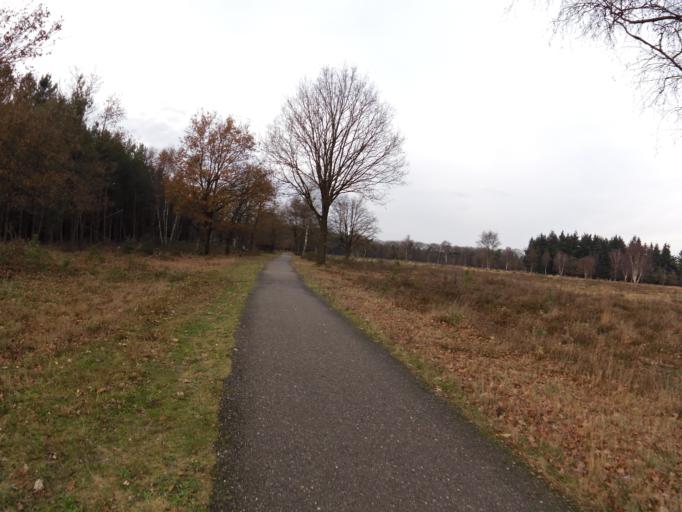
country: NL
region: North Brabant
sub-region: Gemeente Oss
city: Berghem
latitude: 51.7174
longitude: 5.5792
